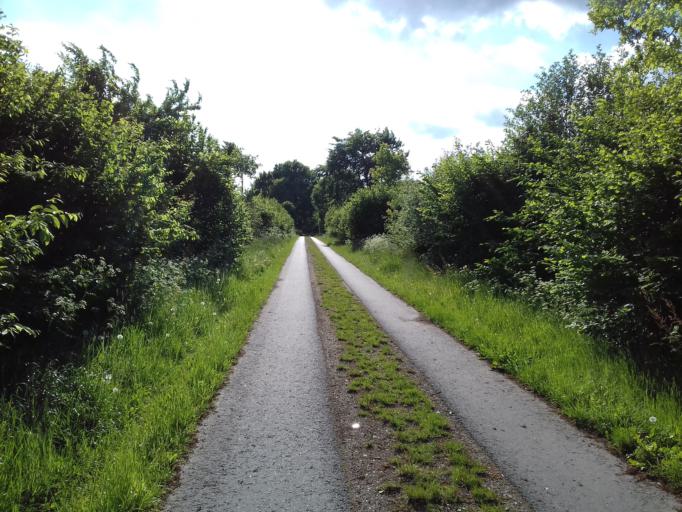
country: DE
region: Schleswig-Holstein
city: Bonebuttel
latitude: 54.0701
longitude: 10.0705
